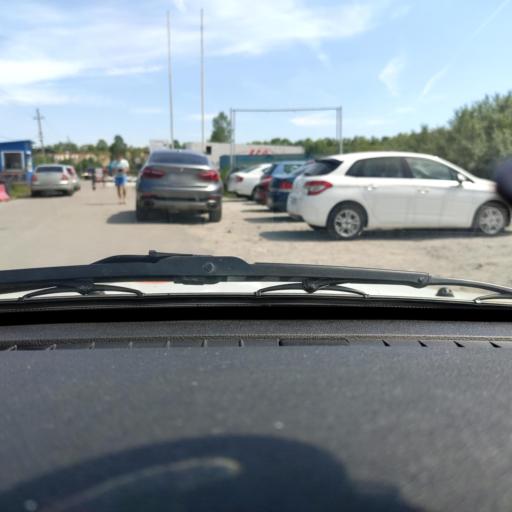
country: RU
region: Voronezj
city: Devitsa
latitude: 51.6225
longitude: 38.9609
